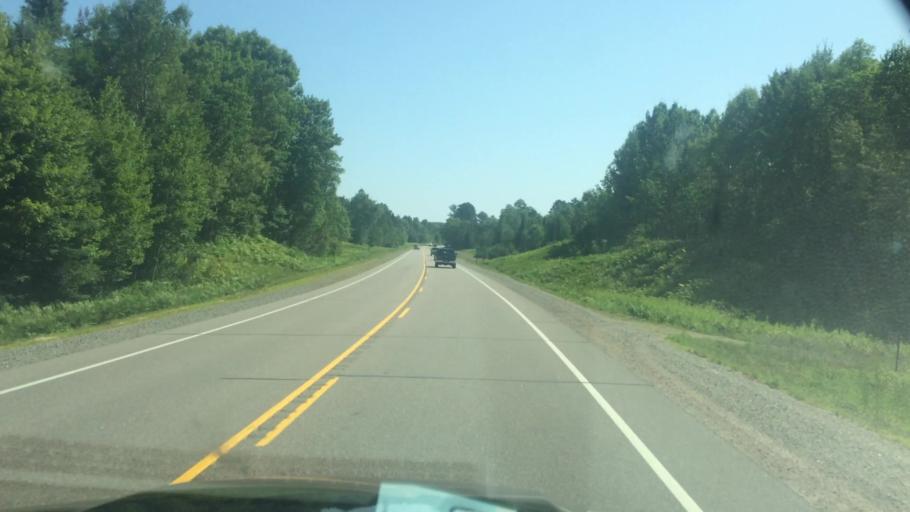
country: US
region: Wisconsin
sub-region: Lincoln County
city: Tomahawk
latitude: 45.5681
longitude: -89.6179
